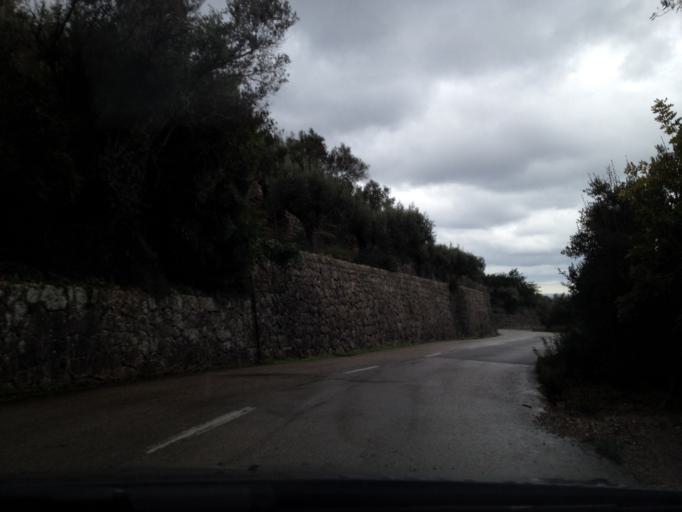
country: ES
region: Balearic Islands
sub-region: Illes Balears
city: Deia
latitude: 39.7743
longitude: 2.6759
